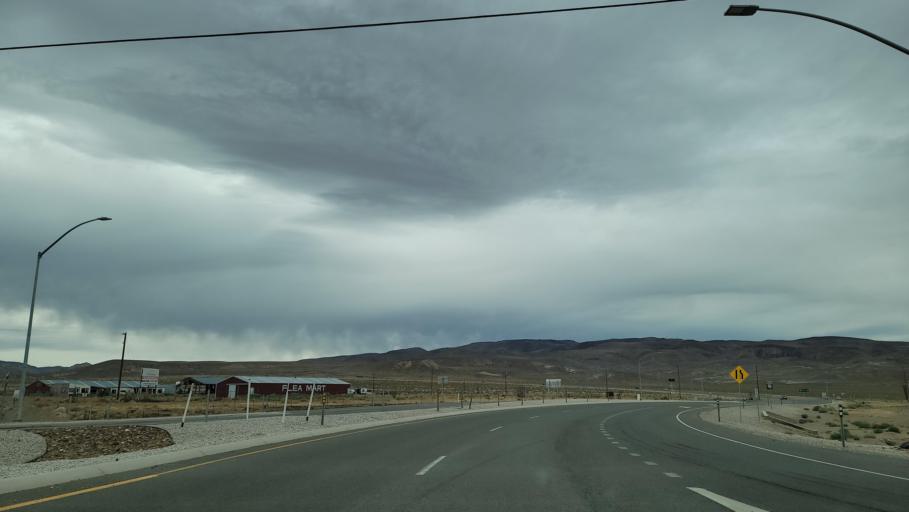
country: US
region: Nevada
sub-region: Lyon County
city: Silver Springs
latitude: 39.4003
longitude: -119.2686
